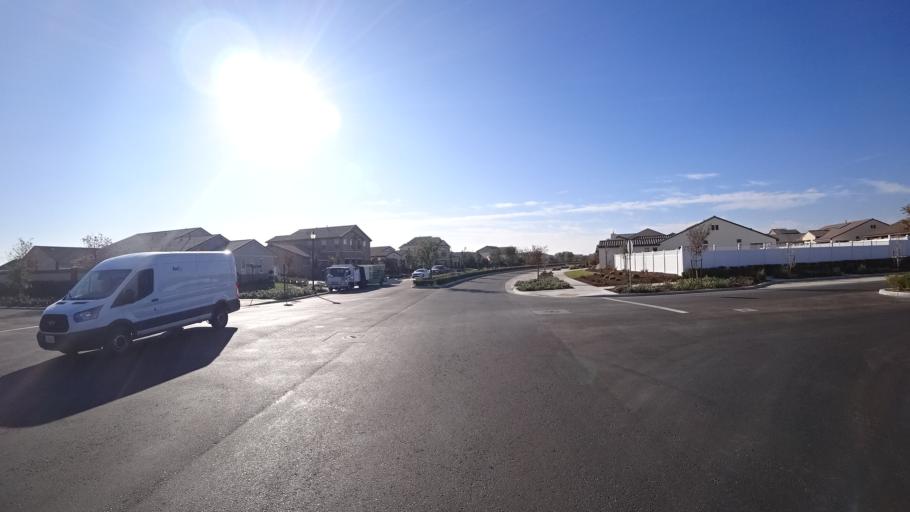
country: US
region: California
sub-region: Kern County
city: Rosedale
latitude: 35.3376
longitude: -119.1526
